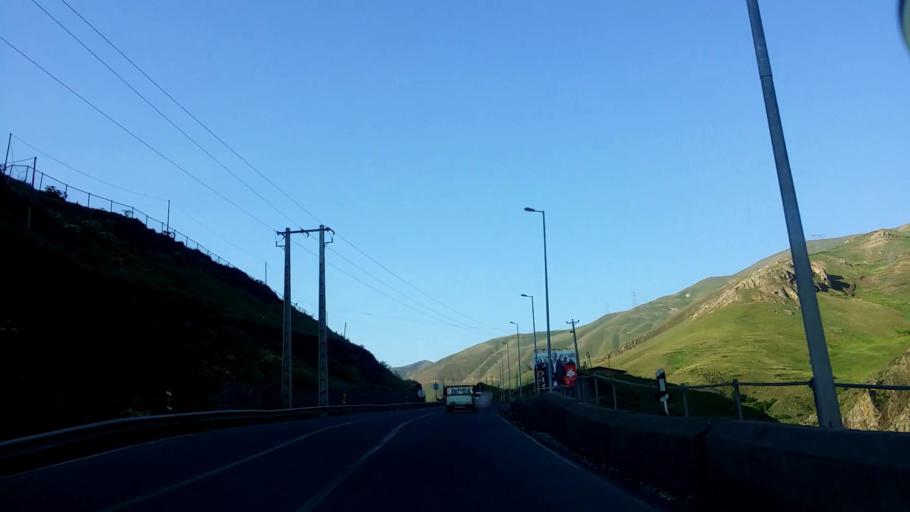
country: IR
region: Tehran
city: Tajrish
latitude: 36.1954
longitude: 51.3211
